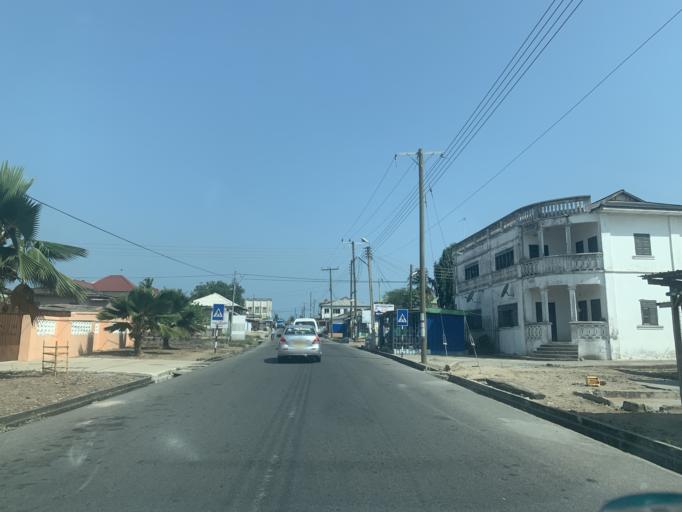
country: GH
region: Central
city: Winneba
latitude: 5.3458
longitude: -0.6285
